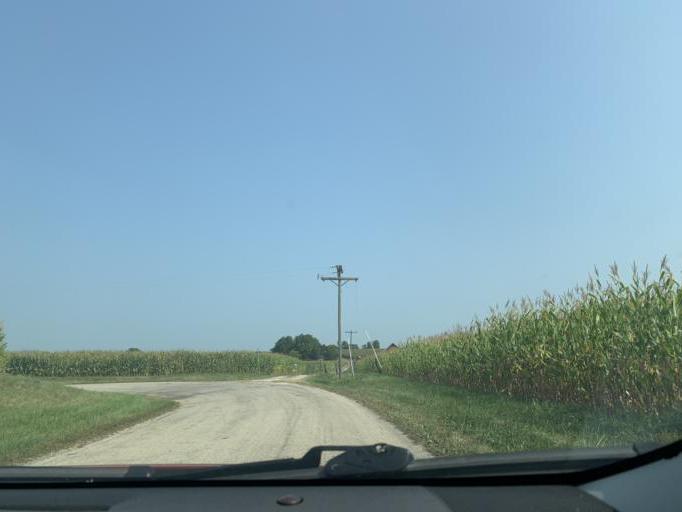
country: US
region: Illinois
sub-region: Whiteside County
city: Morrison
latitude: 41.8693
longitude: -89.8859
